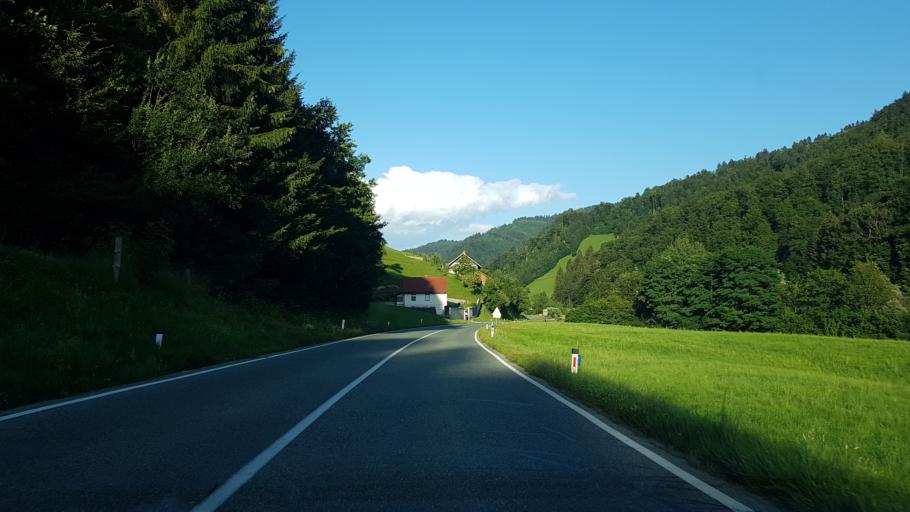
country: SI
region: Gorenja Vas-Poljane
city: Gorenja Vas
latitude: 46.1284
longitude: 14.2111
